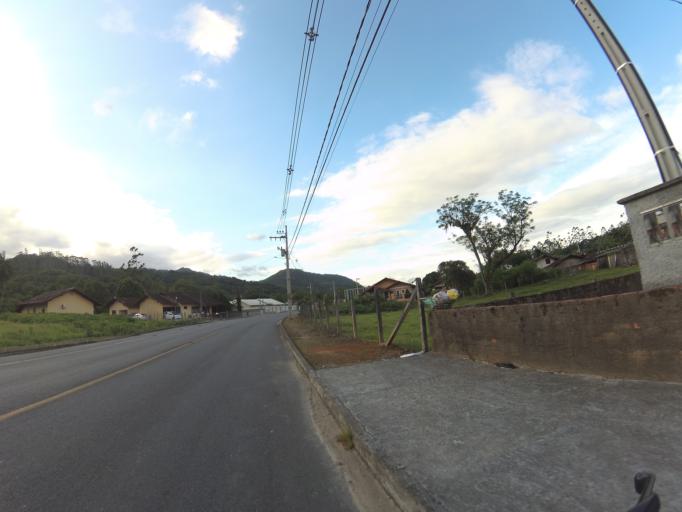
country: BR
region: Santa Catarina
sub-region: Pomerode
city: Pomerode
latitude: -26.8114
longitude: -49.1627
